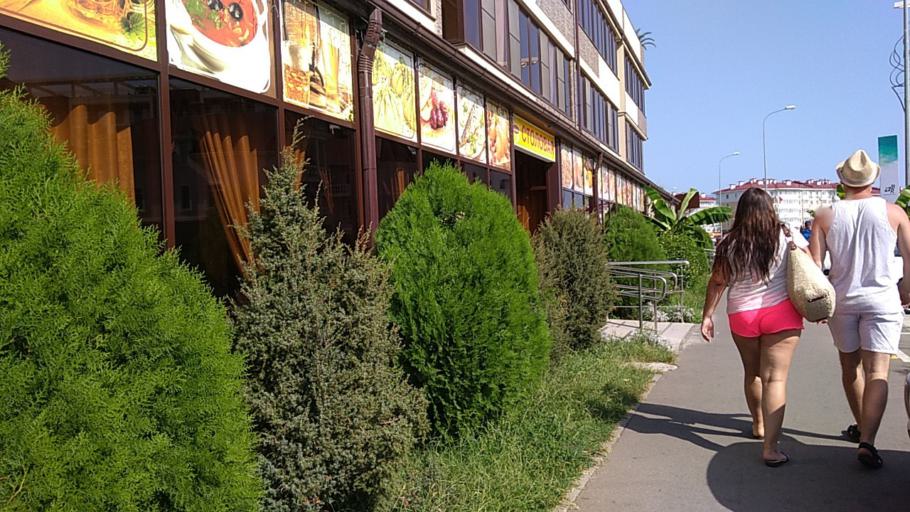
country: RU
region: Krasnodarskiy
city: Adler
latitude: 43.3914
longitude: 39.9880
